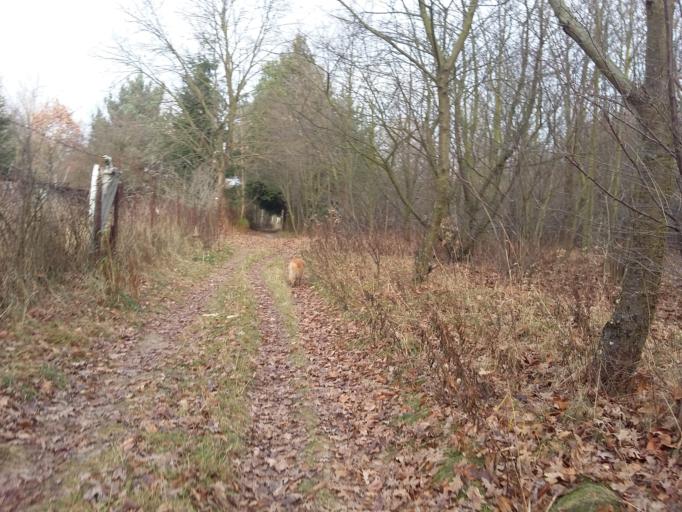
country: PL
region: Lodz Voivodeship
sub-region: Powiat pabianicki
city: Ksawerow
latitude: 51.7346
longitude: 19.4117
